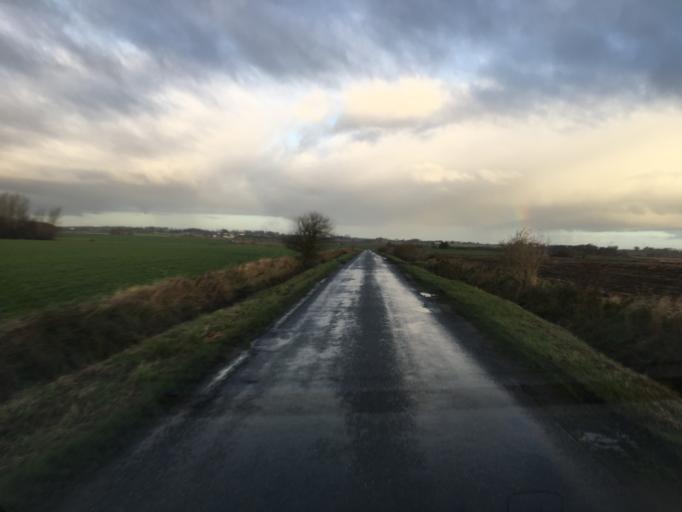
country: DK
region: South Denmark
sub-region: Tonder Kommune
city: Sherrebek
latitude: 55.1376
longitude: 8.8277
